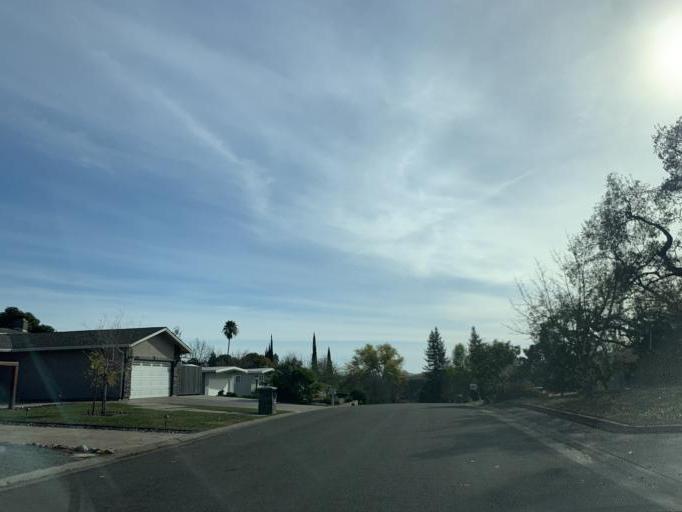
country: US
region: California
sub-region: El Dorado County
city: El Dorado Hills
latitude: 38.6553
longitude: -121.0760
